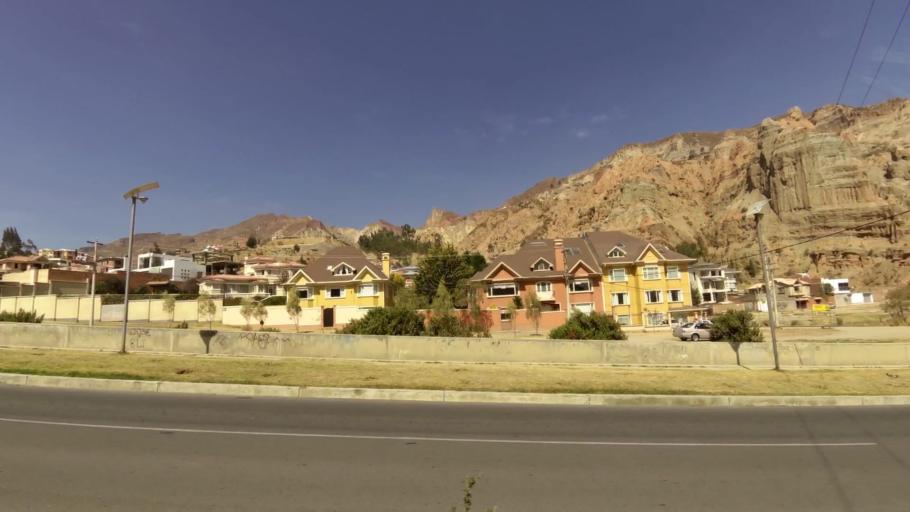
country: BO
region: La Paz
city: La Paz
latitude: -16.5460
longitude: -68.0591
